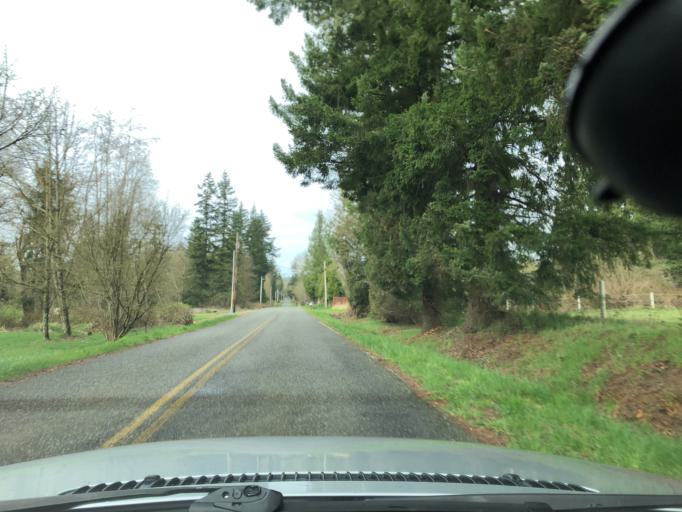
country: CA
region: British Columbia
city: Langley
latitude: 48.9790
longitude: -122.6008
